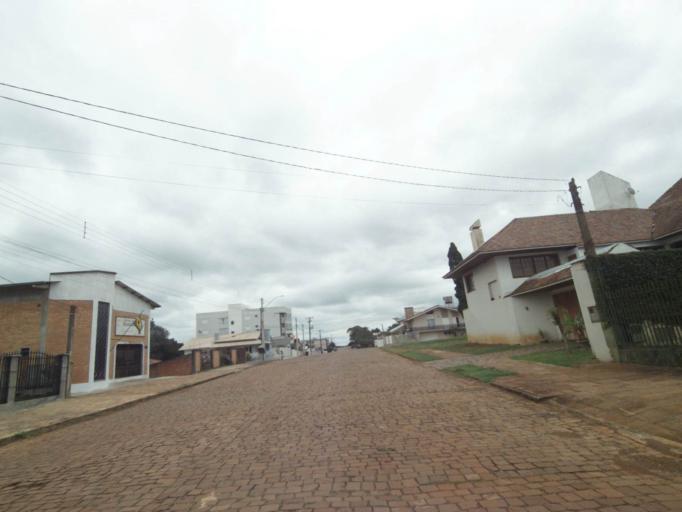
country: BR
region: Rio Grande do Sul
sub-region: Lagoa Vermelha
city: Lagoa Vermelha
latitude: -28.2078
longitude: -51.5188
